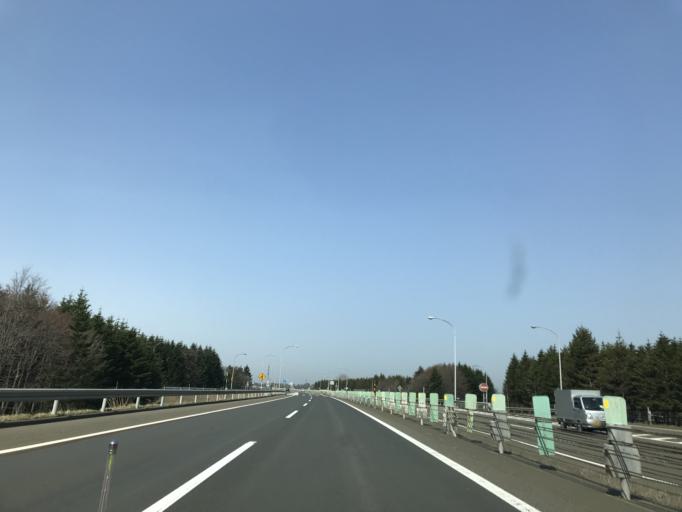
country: JP
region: Hokkaido
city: Ebetsu
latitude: 43.0930
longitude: 141.4990
